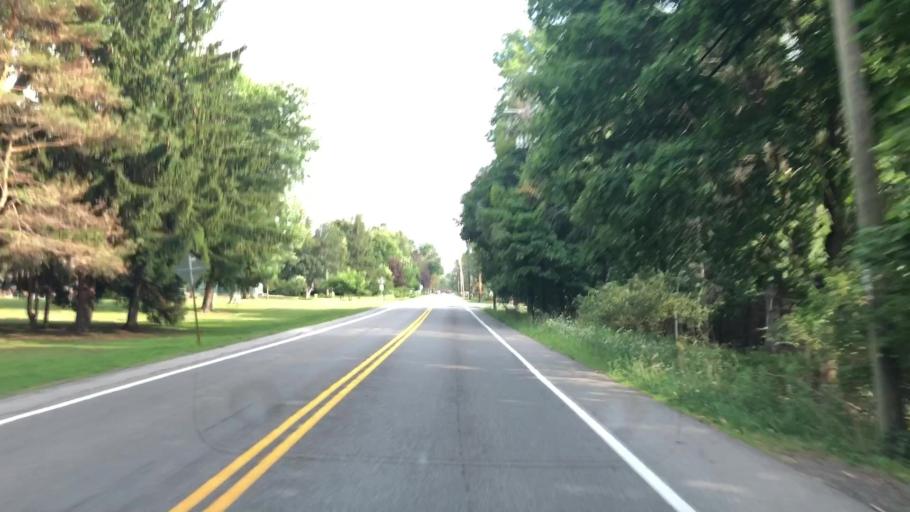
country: US
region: New York
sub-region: Erie County
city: Elma Center
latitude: 42.8466
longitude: -78.6414
